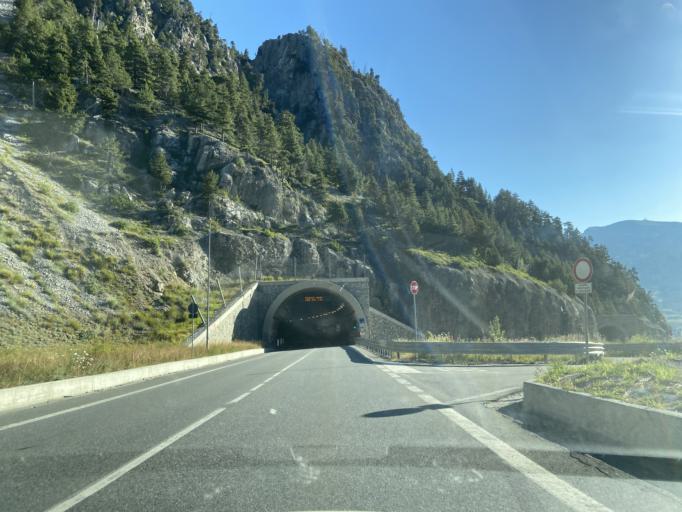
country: IT
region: Piedmont
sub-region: Provincia di Torino
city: Claviere
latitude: 44.9431
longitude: 6.7592
